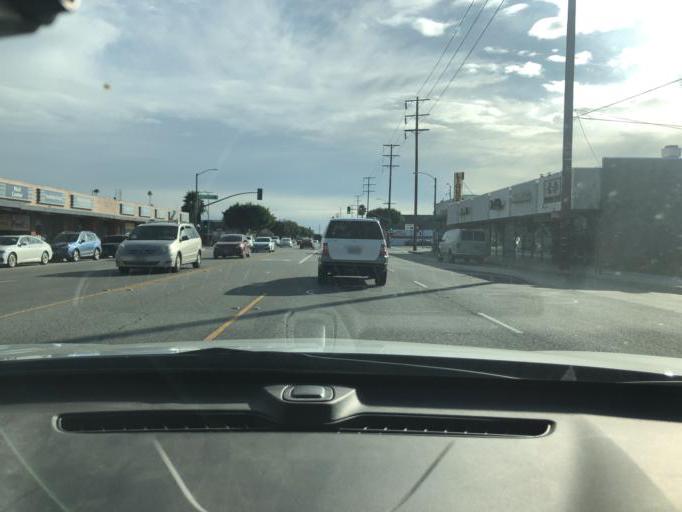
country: US
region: California
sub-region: Los Angeles County
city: Gardena
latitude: 33.8845
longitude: -118.3092
